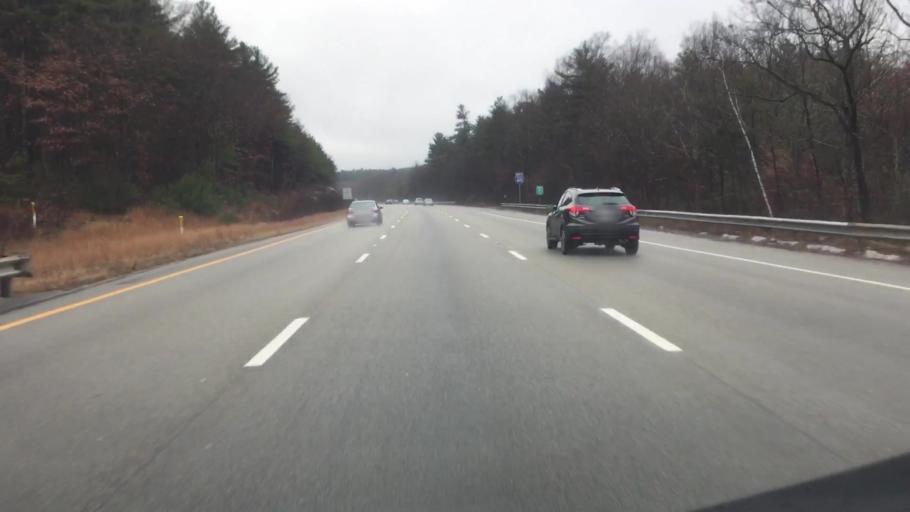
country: US
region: Massachusetts
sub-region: Middlesex County
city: Hopkinton
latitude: 42.2201
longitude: -71.5471
